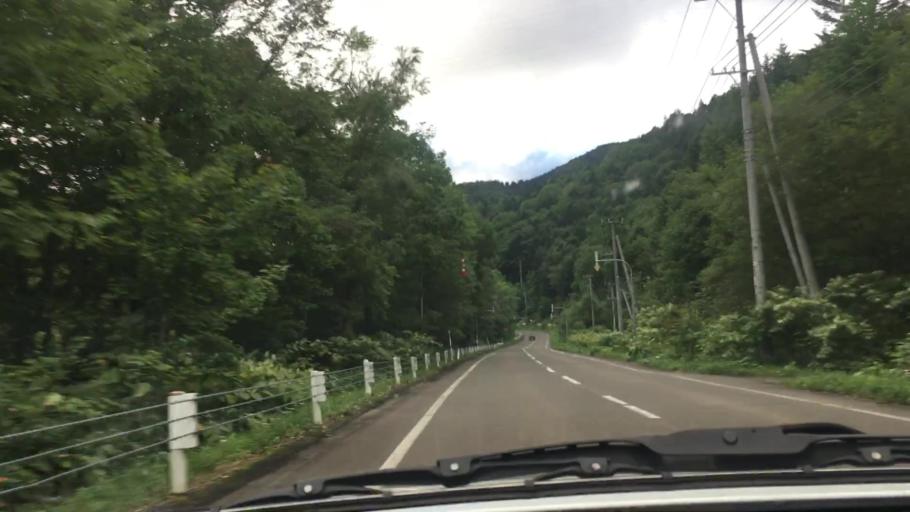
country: JP
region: Hokkaido
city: Shimo-furano
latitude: 43.0467
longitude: 142.5152
